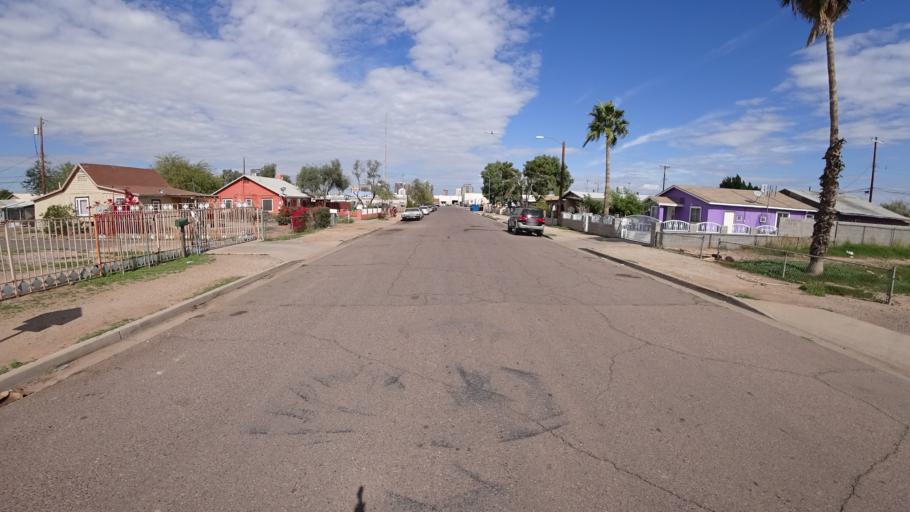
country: US
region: Arizona
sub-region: Maricopa County
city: Phoenix
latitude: 33.4302
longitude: -112.0717
